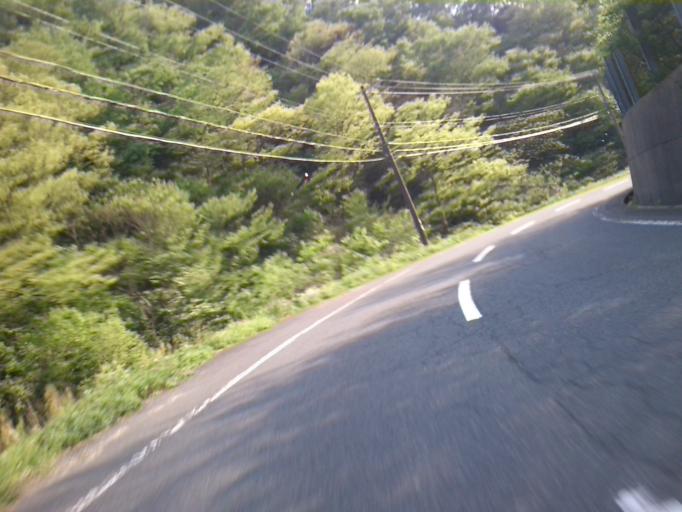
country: JP
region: Kyoto
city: Miyazu
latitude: 35.6936
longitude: 135.1696
